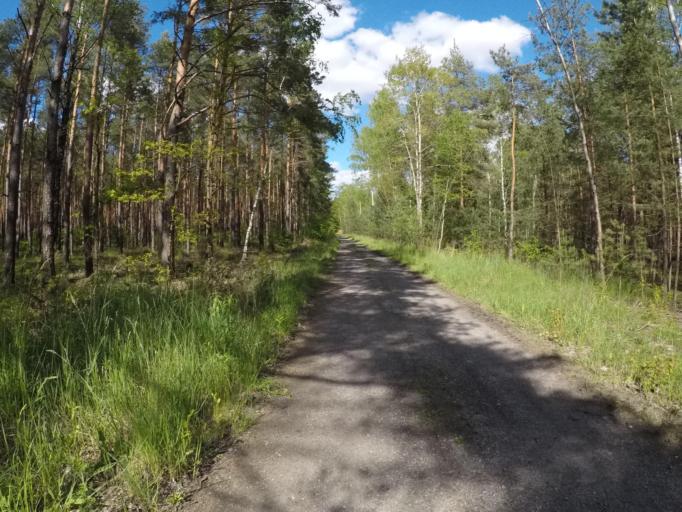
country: PL
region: Swietokrzyskie
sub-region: Powiat kielecki
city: Kostomloty Drugie
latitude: 50.8853
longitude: 20.5332
